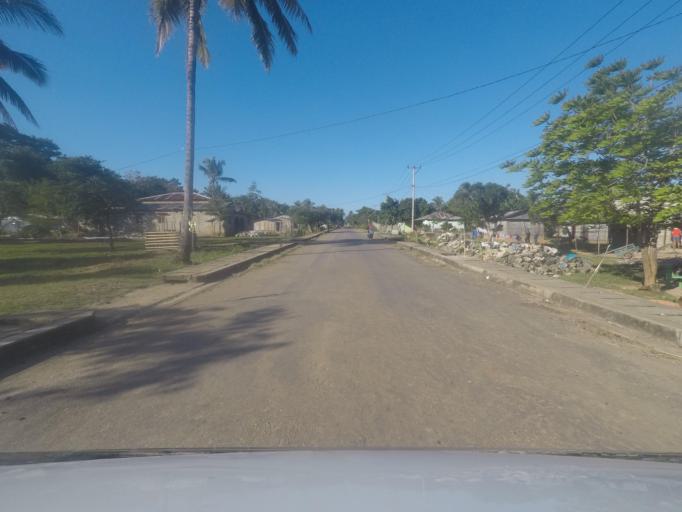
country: TL
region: Lautem
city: Lospalos
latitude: -8.4022
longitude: 127.1804
